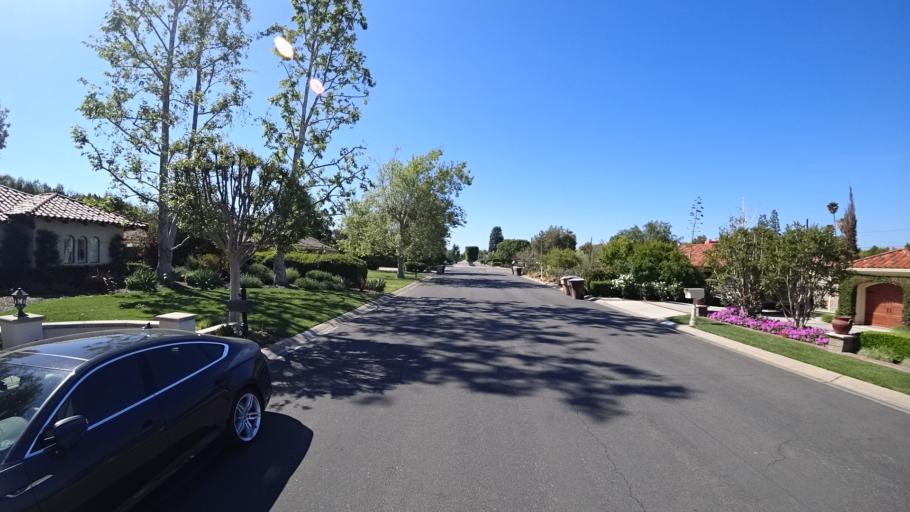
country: US
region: California
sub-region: Orange County
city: Villa Park
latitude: 33.8187
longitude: -117.8064
